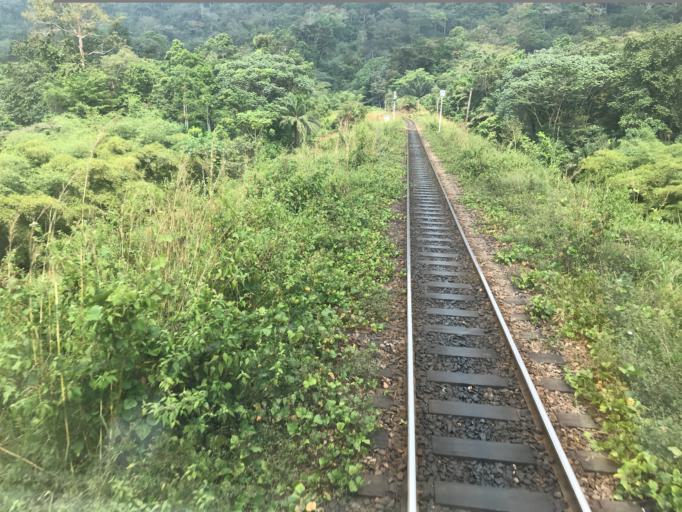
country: CM
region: Centre
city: Eseka
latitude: 3.5769
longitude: 10.8999
